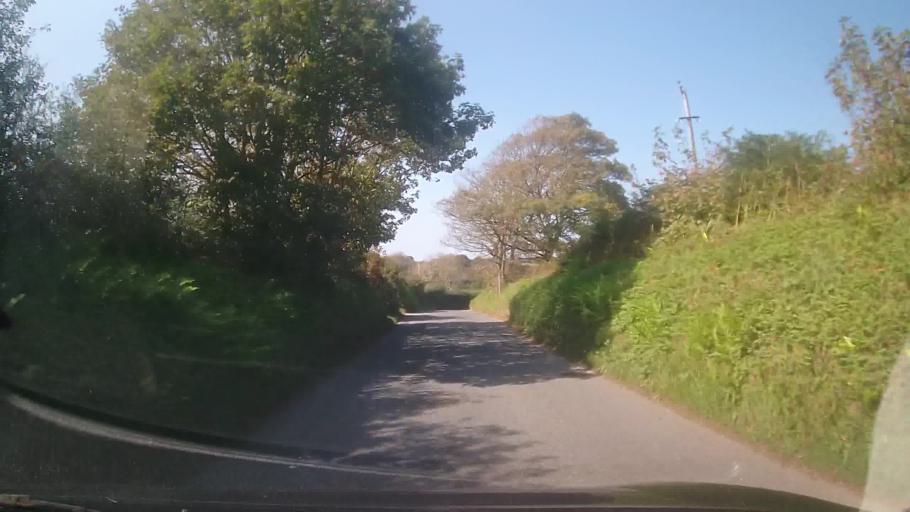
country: GB
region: Wales
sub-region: Pembrokeshire
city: Camrose
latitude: 51.8379
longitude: -4.9813
